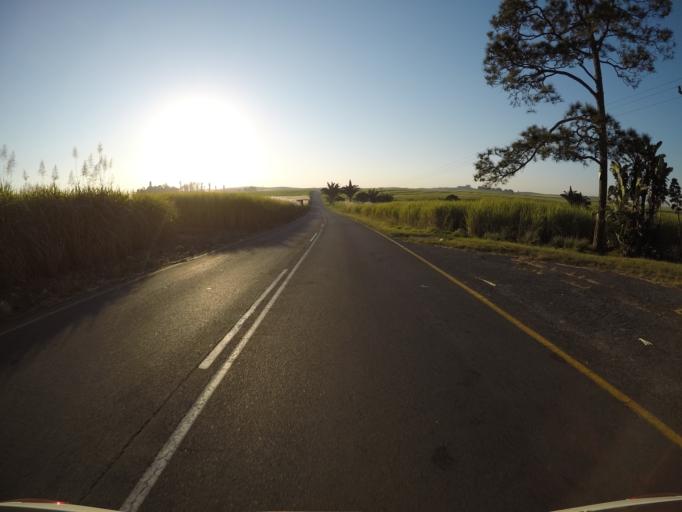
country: ZA
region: KwaZulu-Natal
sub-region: uThungulu District Municipality
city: eSikhawini
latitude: -28.9495
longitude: 31.7131
